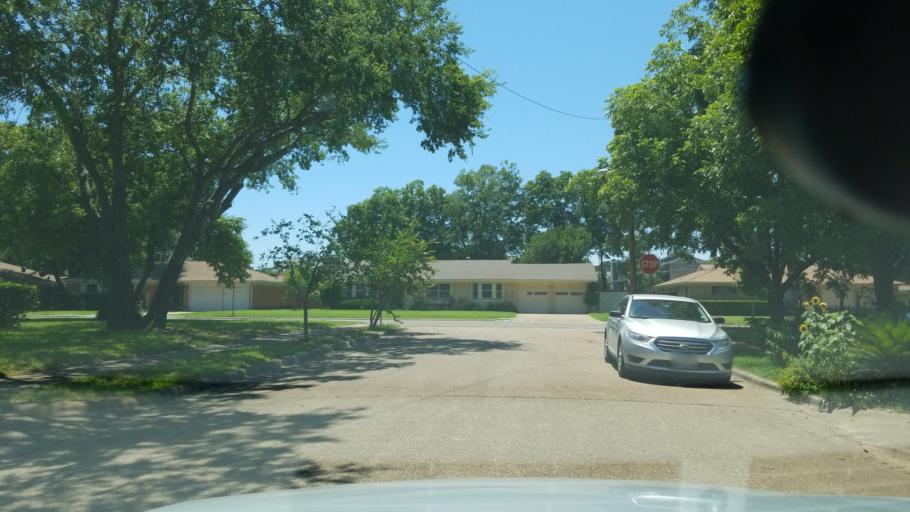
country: US
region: Texas
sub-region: Dallas County
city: Irving
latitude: 32.8279
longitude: -96.9328
